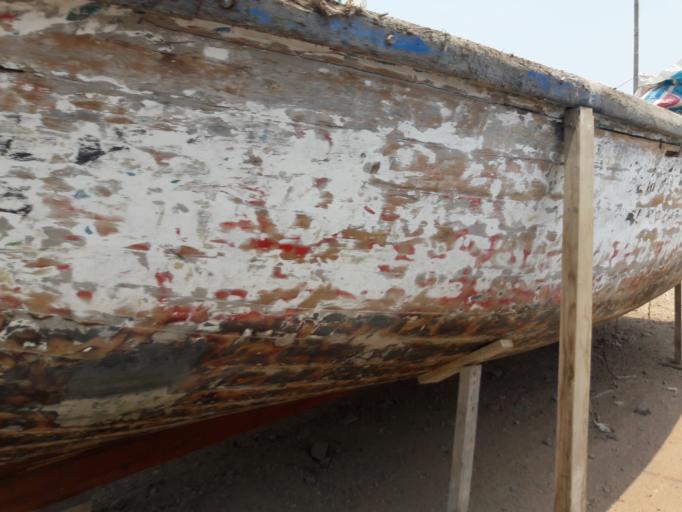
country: PE
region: Lima
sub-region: Lima
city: Santa Rosa
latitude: -11.7702
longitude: -77.1623
